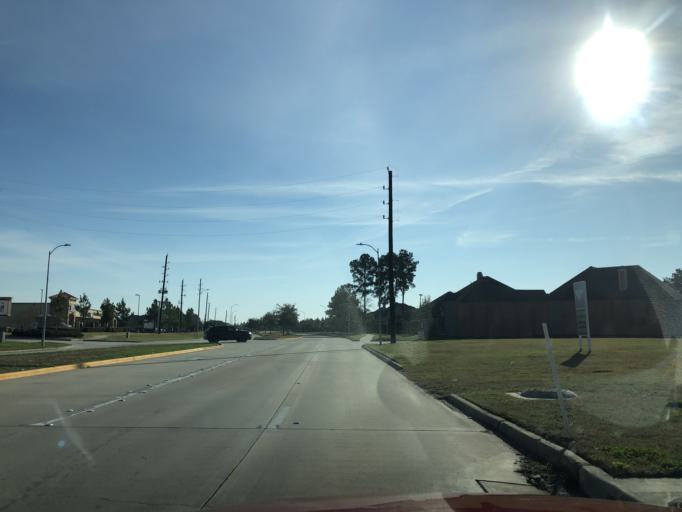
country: US
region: Texas
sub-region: Harris County
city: Tomball
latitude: 30.0555
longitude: -95.5751
